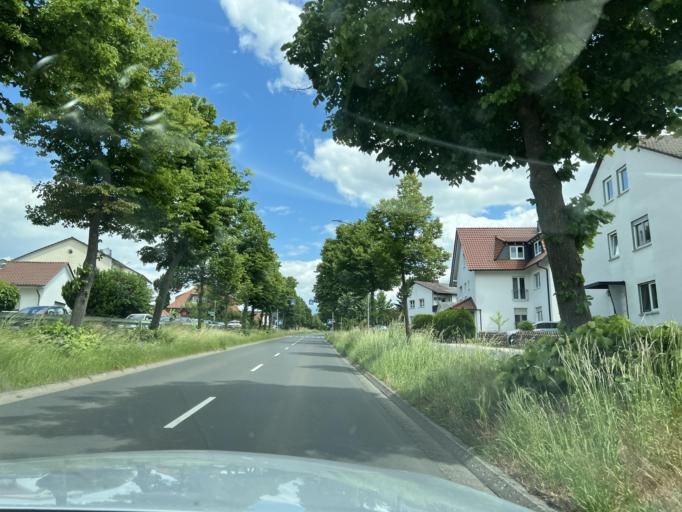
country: DE
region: Hesse
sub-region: Regierungsbezirk Giessen
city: Kirchhain
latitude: 50.8289
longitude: 8.9261
